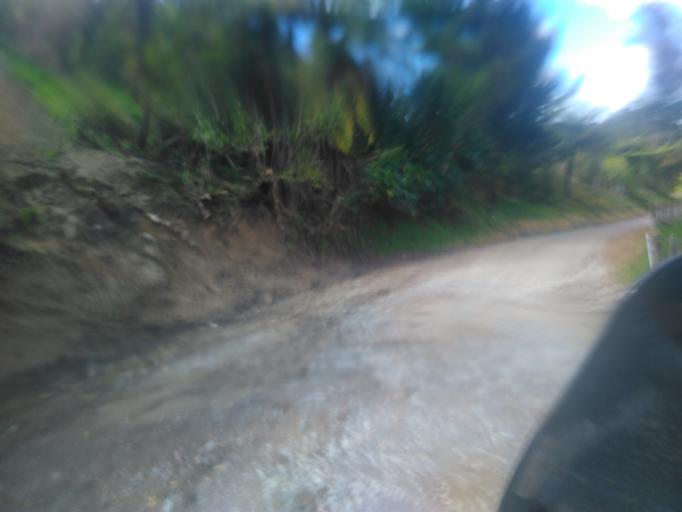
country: NZ
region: Hawke's Bay
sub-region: Wairoa District
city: Wairoa
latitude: -38.7765
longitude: 177.6300
